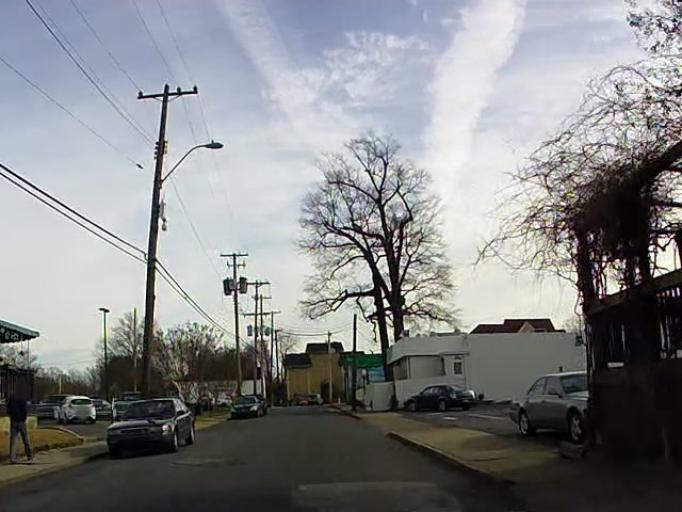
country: US
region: Tennessee
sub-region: Shelby County
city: Memphis
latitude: 35.1372
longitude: -89.9913
